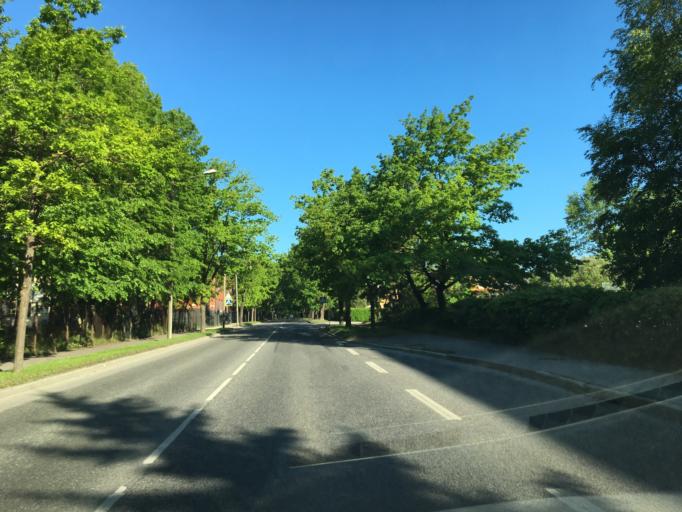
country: EE
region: Tartu
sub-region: Tartu linn
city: Tartu
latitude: 58.3909
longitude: 26.7252
